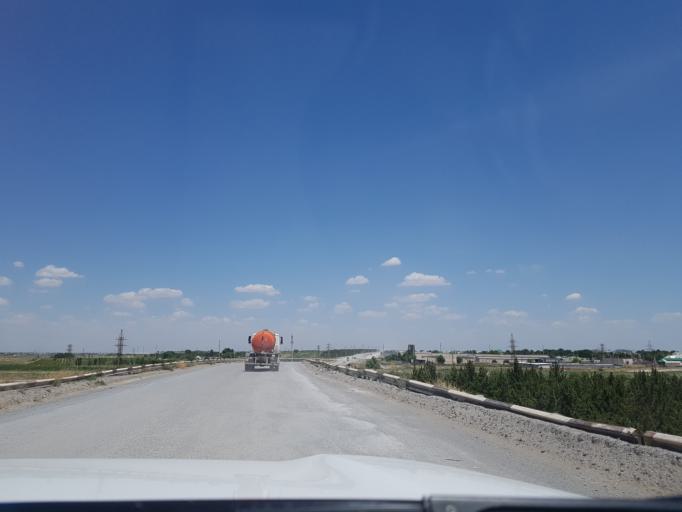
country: TM
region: Ahal
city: Abadan
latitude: 38.1720
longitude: 57.9414
